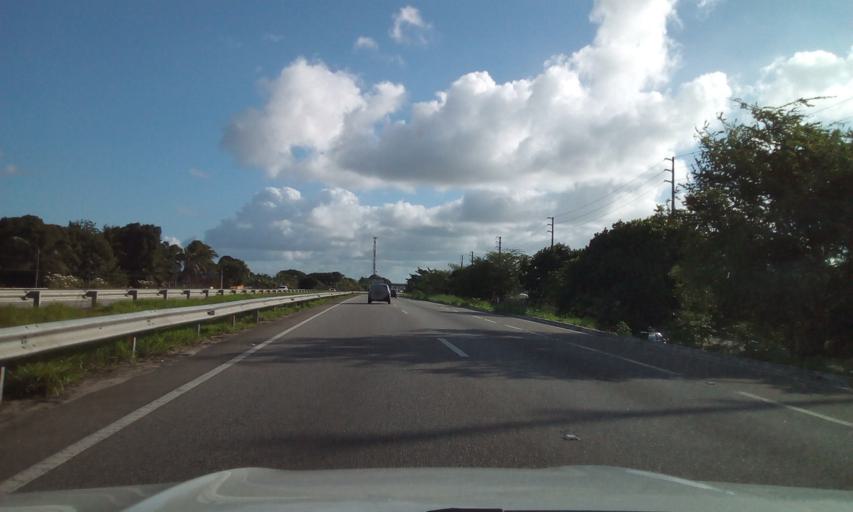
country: BR
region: Paraiba
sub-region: Bayeux
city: Bayeux
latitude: -7.1289
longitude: -34.9530
